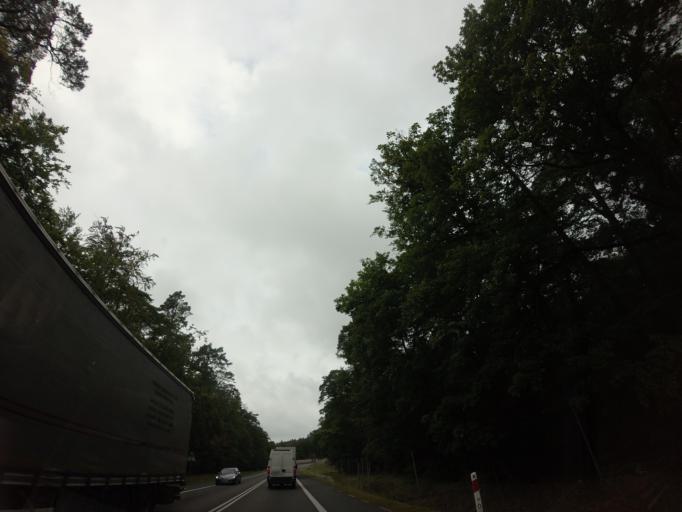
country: PL
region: West Pomeranian Voivodeship
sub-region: Powiat kamienski
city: Miedzyzdroje
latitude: 53.9016
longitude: 14.4532
